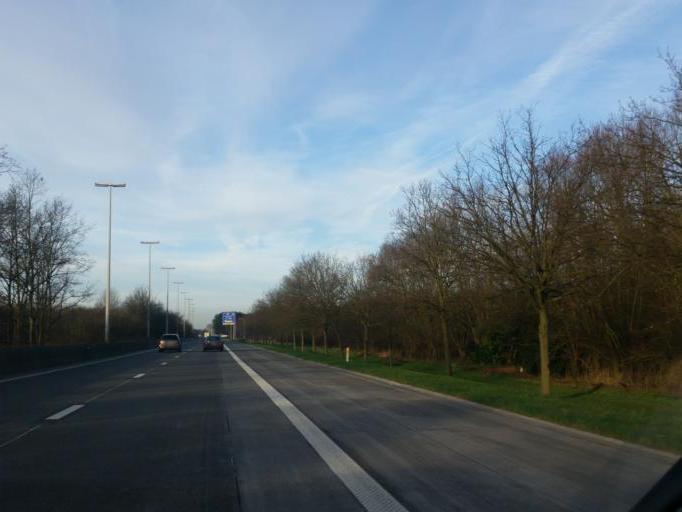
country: BE
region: Flanders
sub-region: Provincie Oost-Vlaanderen
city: Wachtebeke
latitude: 51.1896
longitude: 3.8472
